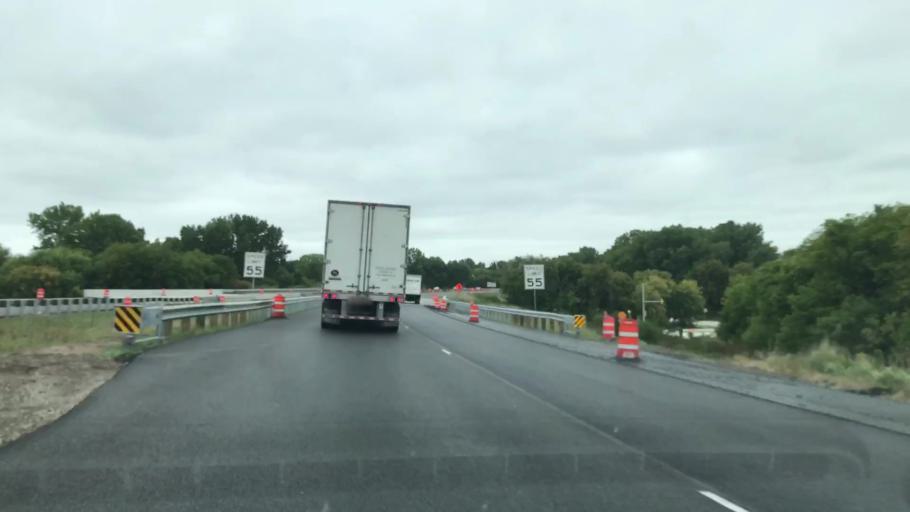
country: US
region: Wisconsin
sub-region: Brown County
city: Suamico
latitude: 44.6363
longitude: -88.0460
